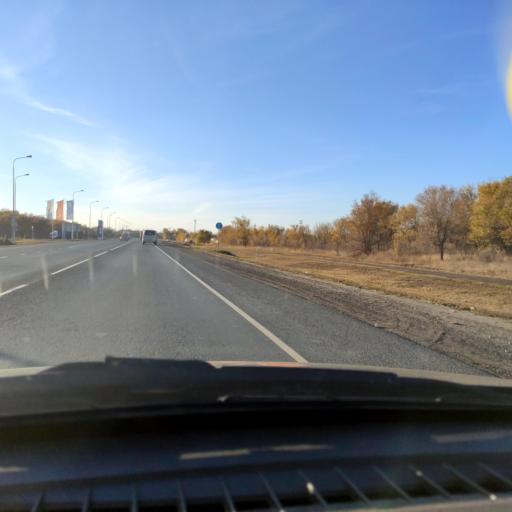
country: RU
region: Samara
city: Varlamovo
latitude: 53.1913
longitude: 48.3480
